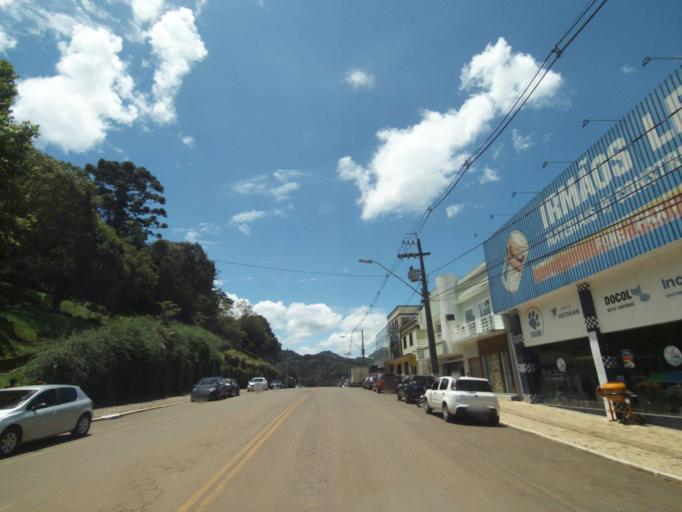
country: BR
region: Parana
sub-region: Uniao Da Vitoria
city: Uniao da Vitoria
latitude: -26.1617
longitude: -51.5549
